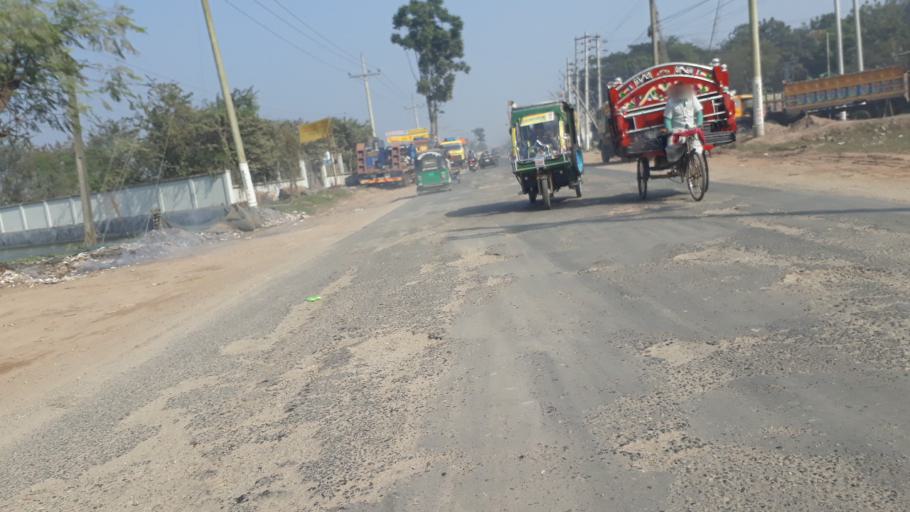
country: BD
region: Khulna
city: Kushtia
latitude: 23.8818
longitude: 89.0955
